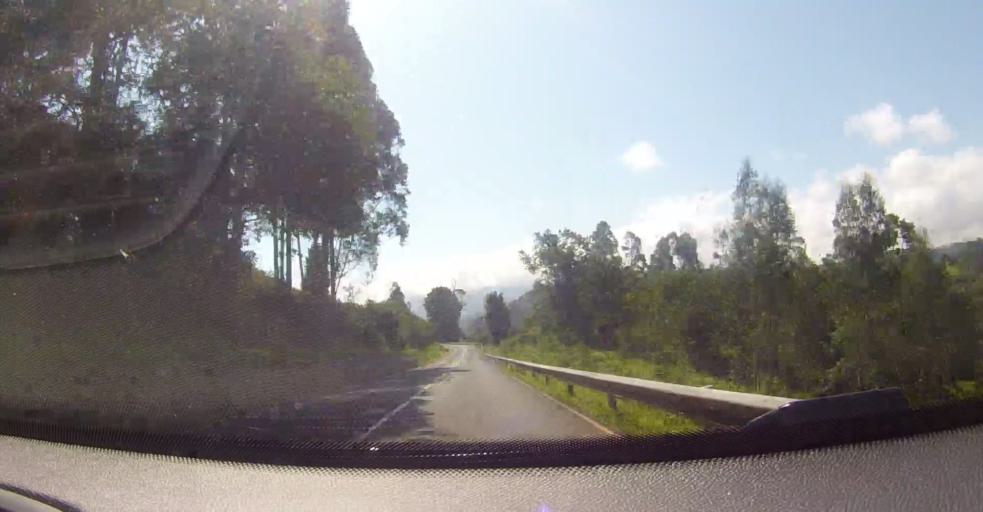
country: ES
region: Asturias
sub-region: Province of Asturias
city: Colunga
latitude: 43.4951
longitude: -5.3277
